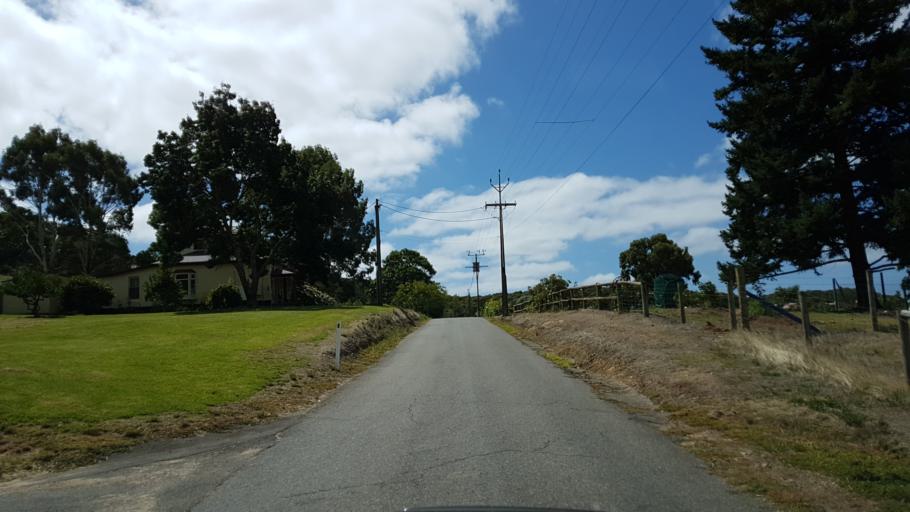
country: AU
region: South Australia
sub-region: Adelaide Hills
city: Crafers
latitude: -34.9768
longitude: 138.7172
